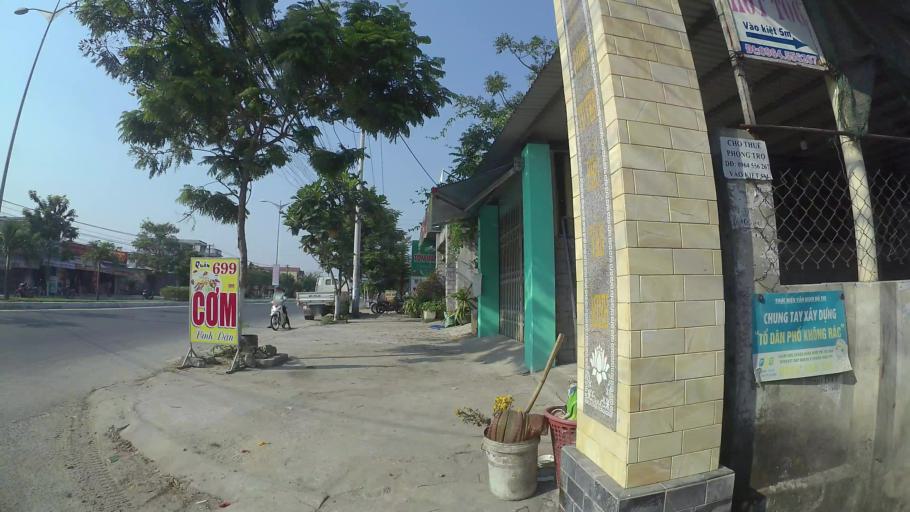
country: VN
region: Quang Nam
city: Quang Nam
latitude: 15.9469
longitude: 108.2548
